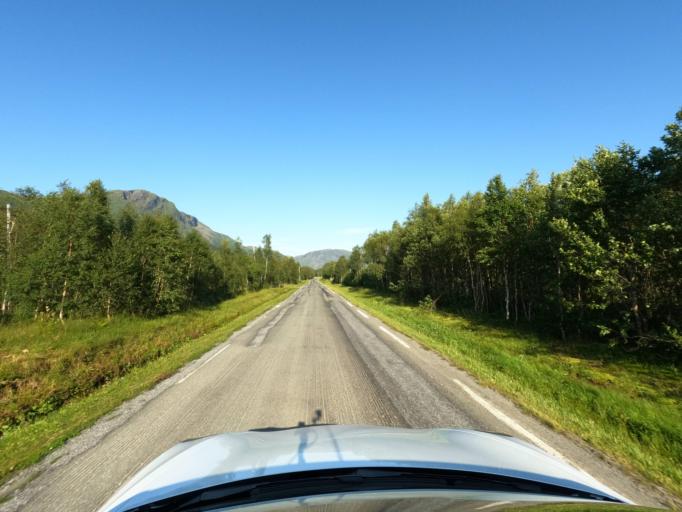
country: NO
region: Nordland
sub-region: Narvik
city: Bjerkvik
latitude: 68.5579
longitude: 17.6333
